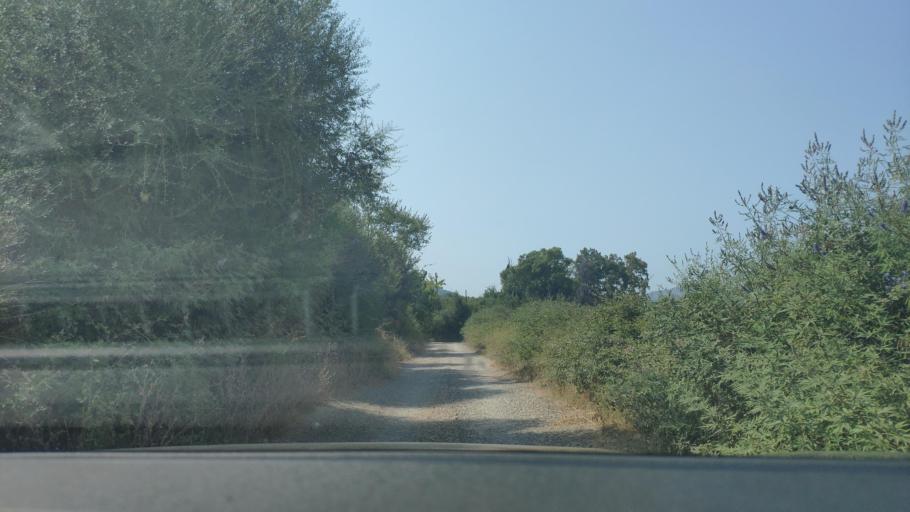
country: GR
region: West Greece
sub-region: Nomos Aitolias kai Akarnanias
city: Fitiai
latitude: 38.7155
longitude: 21.1998
